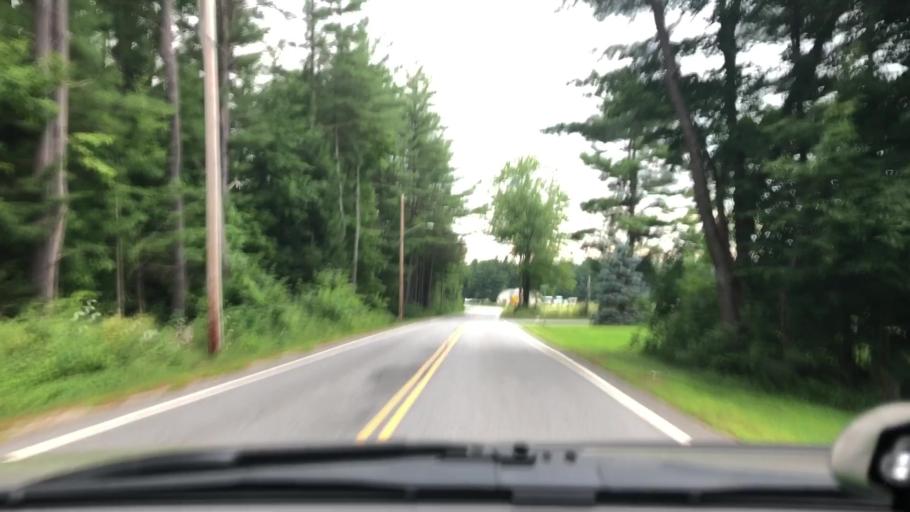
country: US
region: New York
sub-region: Saratoga County
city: Corinth
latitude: 43.2216
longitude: -73.8138
